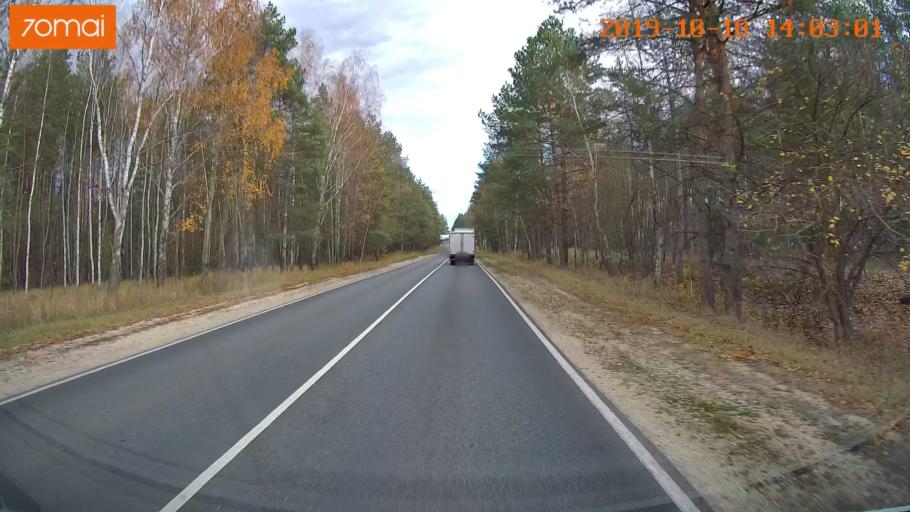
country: RU
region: Rjazan
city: Spas-Klepiki
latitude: 55.1155
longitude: 40.1182
